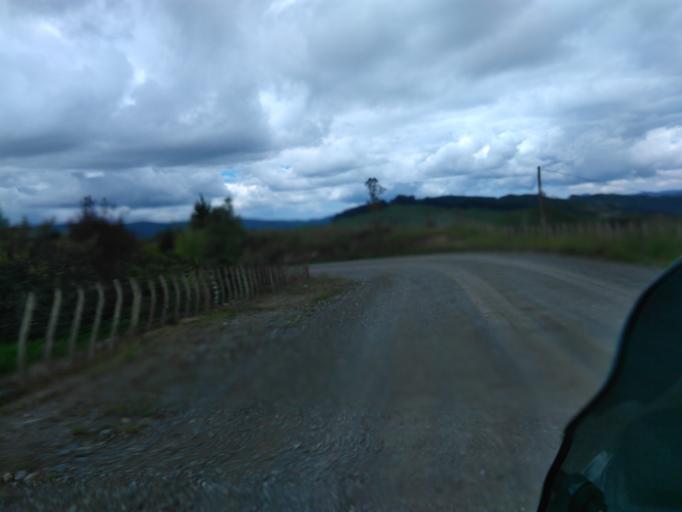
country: NZ
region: Gisborne
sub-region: Gisborne District
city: Gisborne
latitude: -38.0498
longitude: 178.0526
